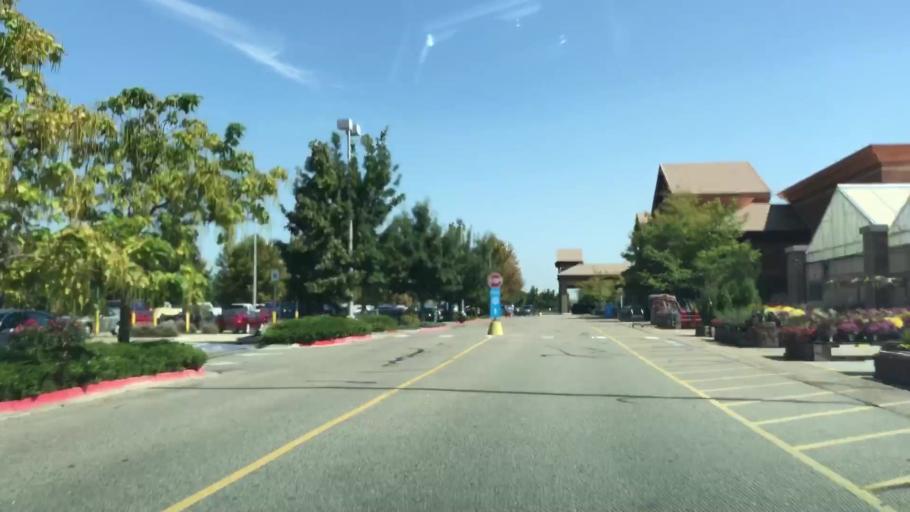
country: US
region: Colorado
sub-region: Larimer County
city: Loveland
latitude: 40.4055
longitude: -105.0384
